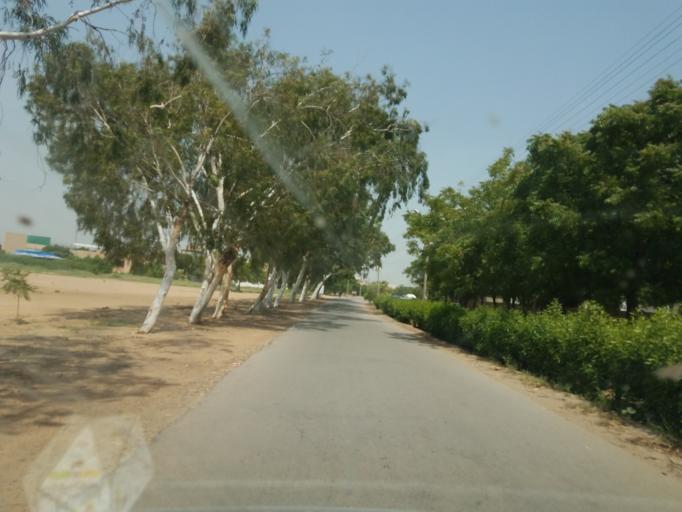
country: PK
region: Sindh
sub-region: Karachi District
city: Karachi
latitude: 24.9369
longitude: 67.1100
